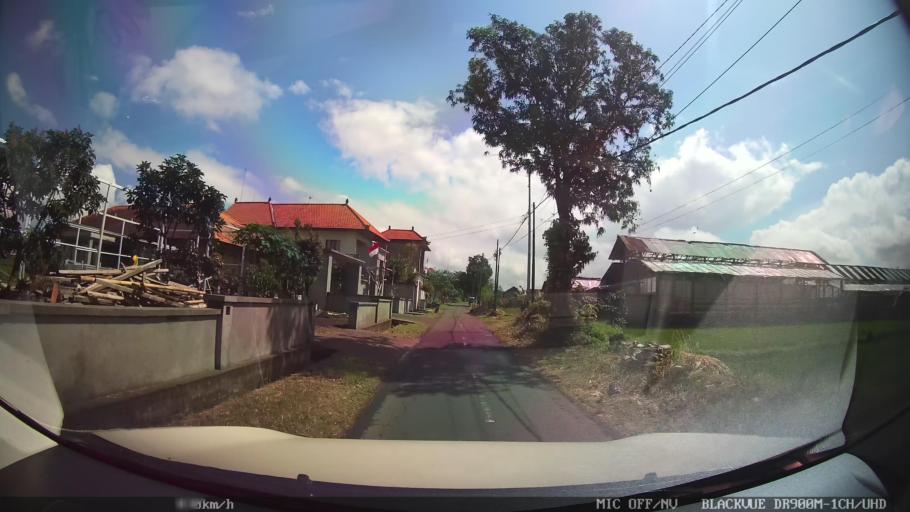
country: ID
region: Bali
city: Banjar Sedang
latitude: -8.5555
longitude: 115.2691
